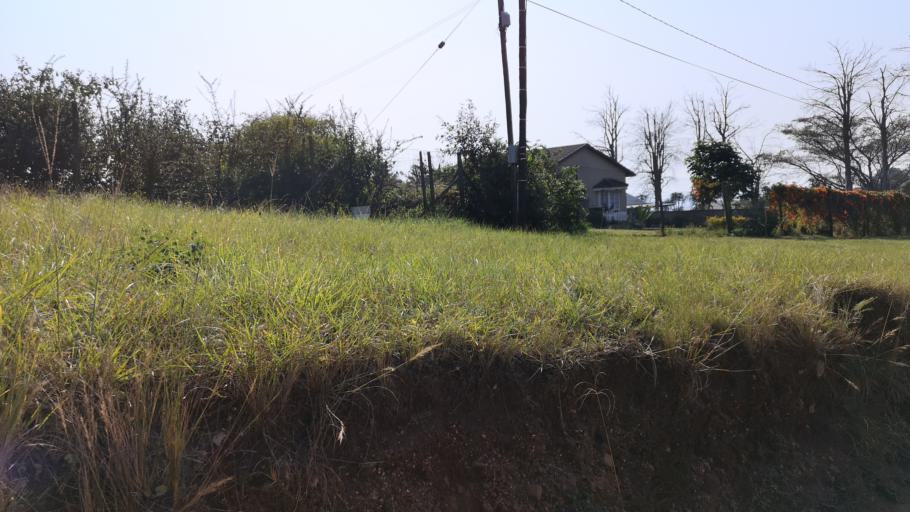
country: ZA
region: KwaZulu-Natal
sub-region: eThekwini Metropolitan Municipality
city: Mpumalanga
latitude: -29.7366
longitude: 30.6833
